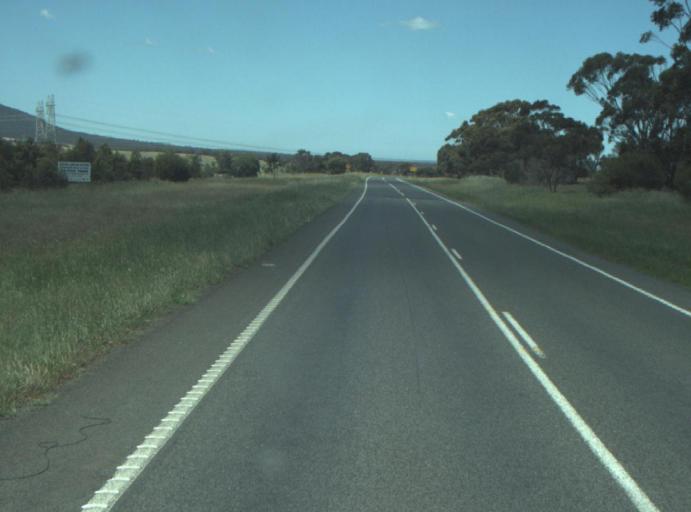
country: AU
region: Victoria
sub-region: Greater Geelong
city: Lara
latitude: -37.8994
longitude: 144.3698
